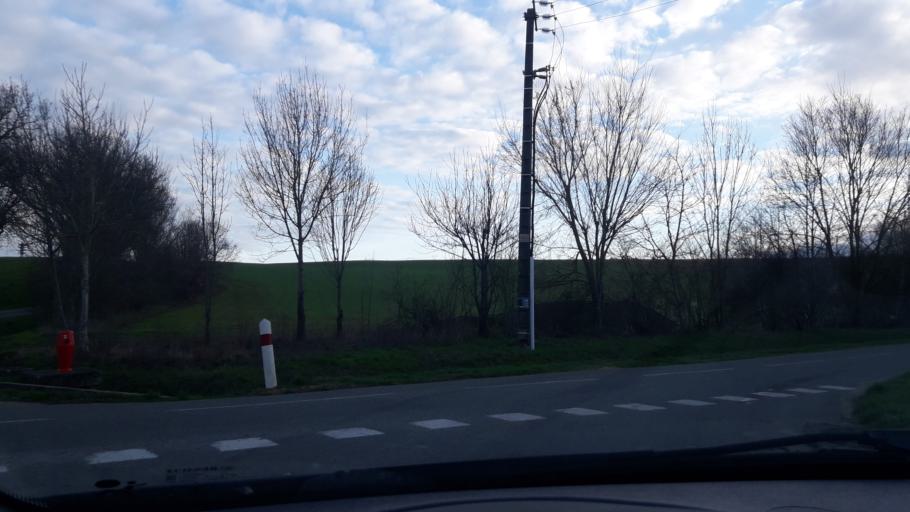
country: FR
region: Midi-Pyrenees
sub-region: Departement du Gers
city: Pujaudran
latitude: 43.6672
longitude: 1.0931
